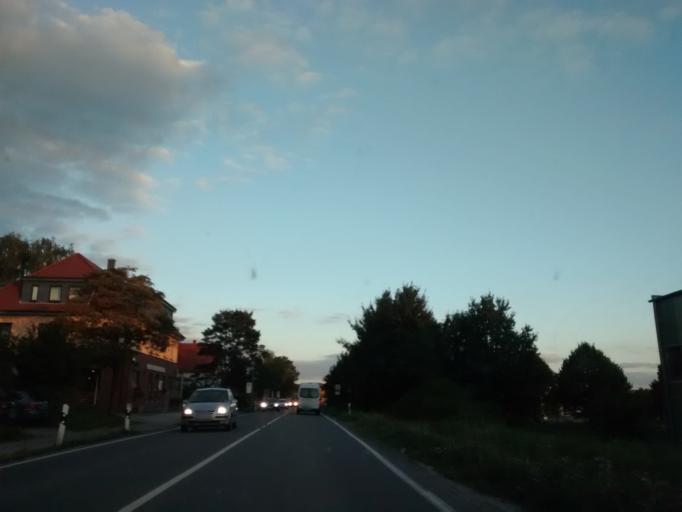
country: DE
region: North Rhine-Westphalia
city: Halle
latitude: 52.0687
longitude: 8.3434
